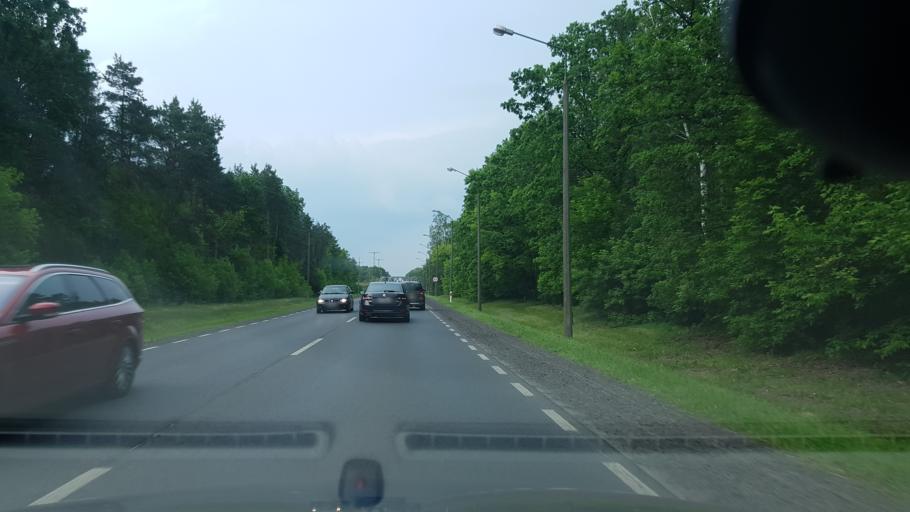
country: PL
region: Masovian Voivodeship
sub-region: Powiat legionowski
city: Wieliszew
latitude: 52.4330
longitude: 20.9863
